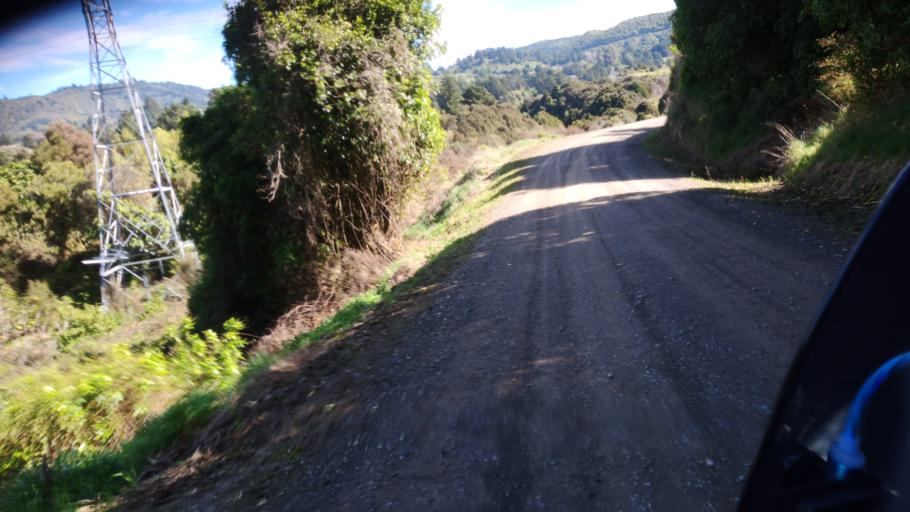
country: NZ
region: Hawke's Bay
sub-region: Wairoa District
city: Wairoa
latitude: -38.8190
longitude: 177.1586
